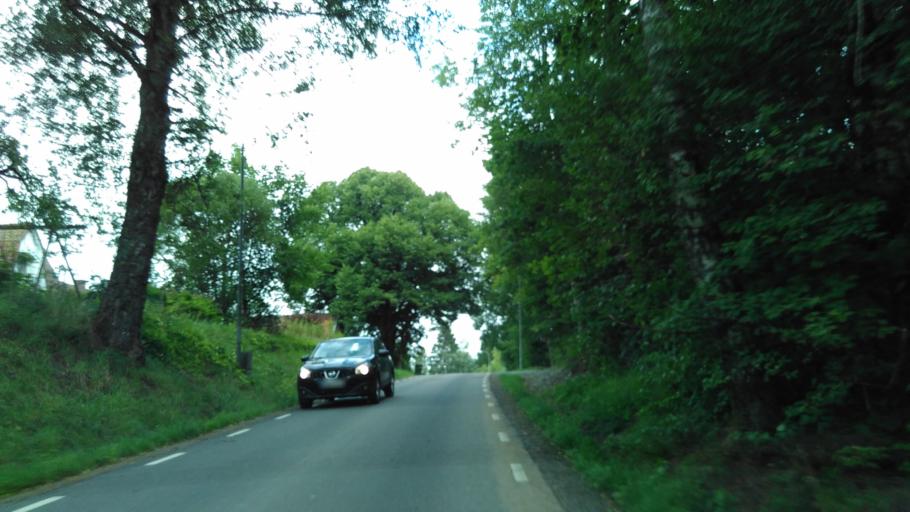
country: SE
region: Vaestra Goetaland
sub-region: Marks Kommun
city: Fritsla
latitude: 57.5654
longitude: 12.7835
